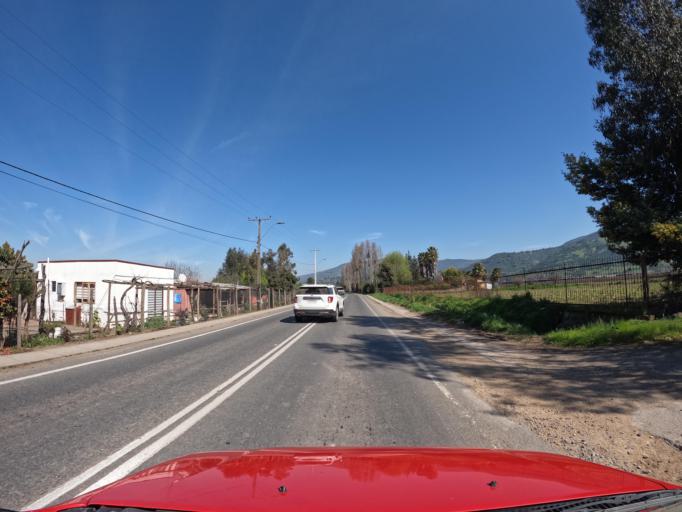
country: CL
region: Maule
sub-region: Provincia de Curico
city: Rauco
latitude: -34.9797
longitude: -71.4033
